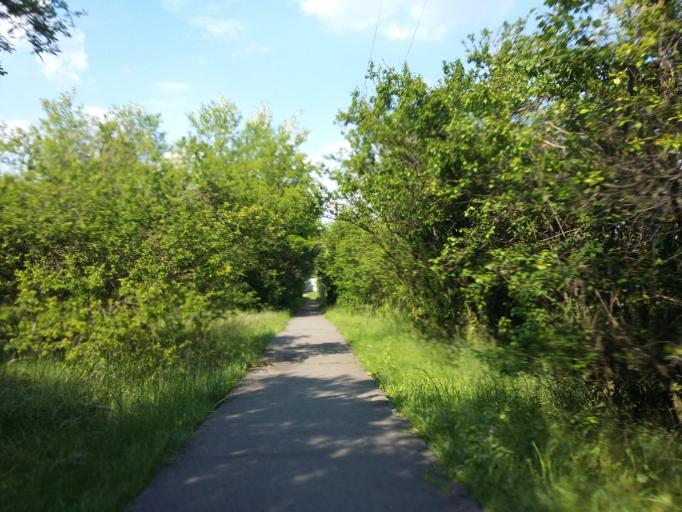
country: SK
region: Bratislavsky
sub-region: Okres Malacky
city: Malacky
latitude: 48.5079
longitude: 17.0163
